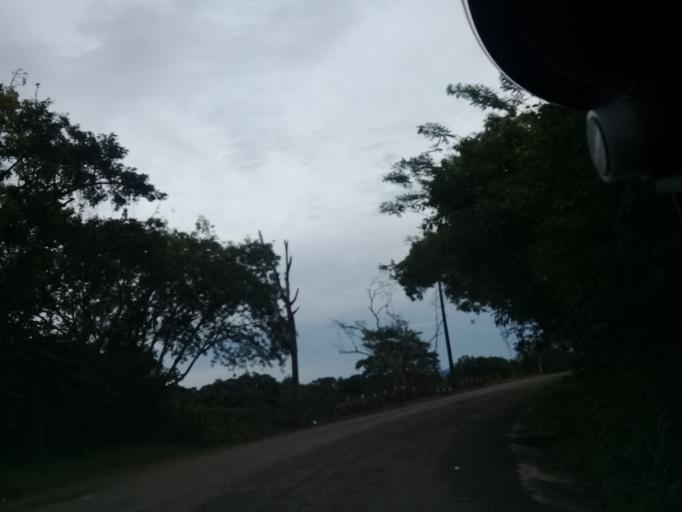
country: MX
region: Hidalgo
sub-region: Huejutla de Reyes
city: Chalahuiyapa
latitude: 21.1995
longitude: -98.3331
